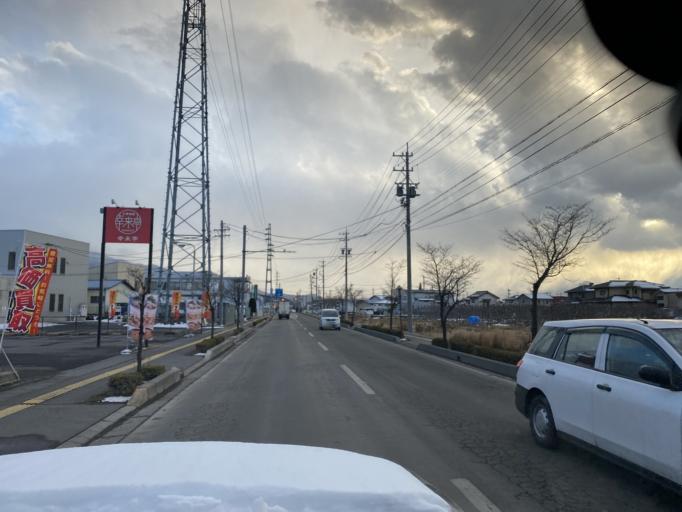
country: JP
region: Nagano
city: Nagano-shi
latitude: 36.6357
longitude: 138.2406
